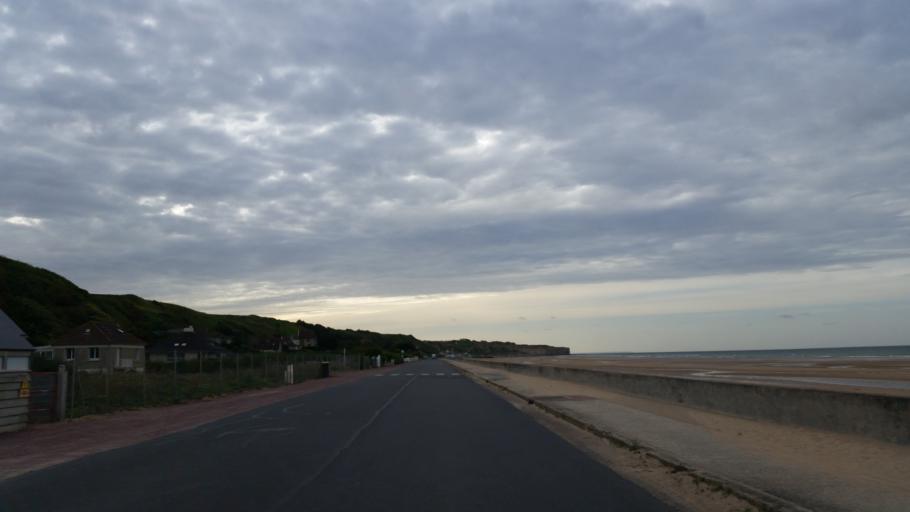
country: FR
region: Lower Normandy
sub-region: Departement du Calvados
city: Le Molay-Littry
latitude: 49.3733
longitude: -0.8868
